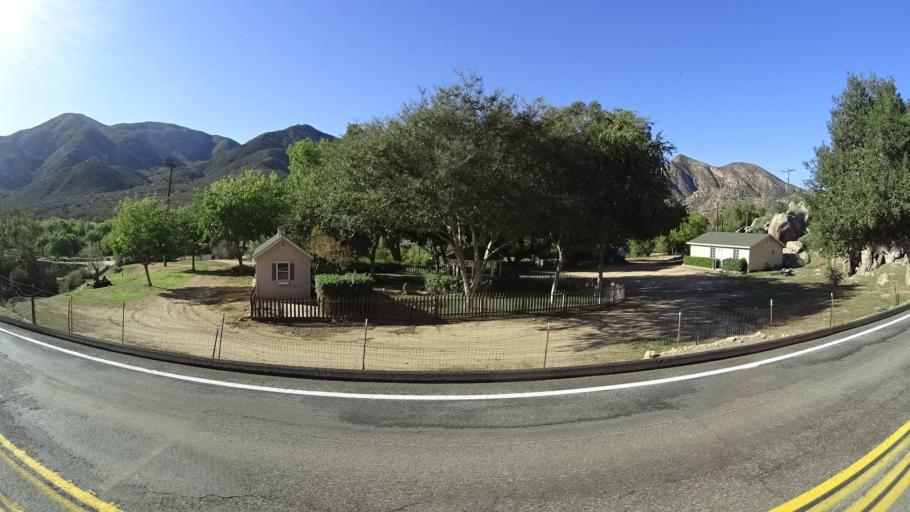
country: MX
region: Baja California
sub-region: Tecate
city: Lomas de Santa Anita
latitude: 32.6124
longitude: -116.7086
